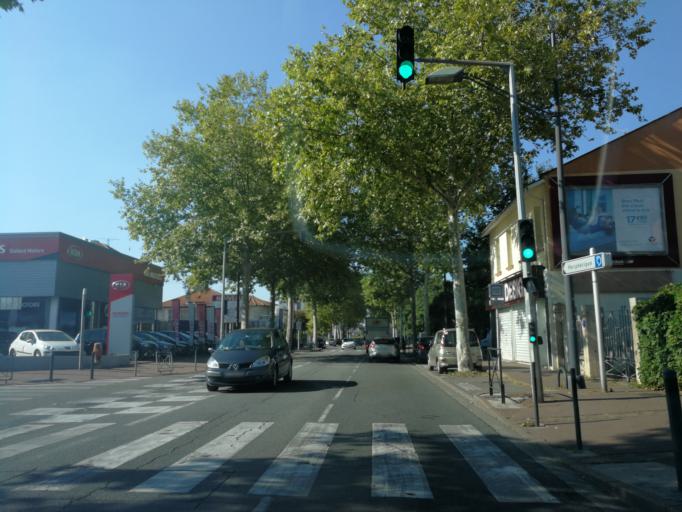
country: FR
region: Midi-Pyrenees
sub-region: Departement de la Haute-Garonne
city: Toulouse
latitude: 43.6349
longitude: 1.4310
